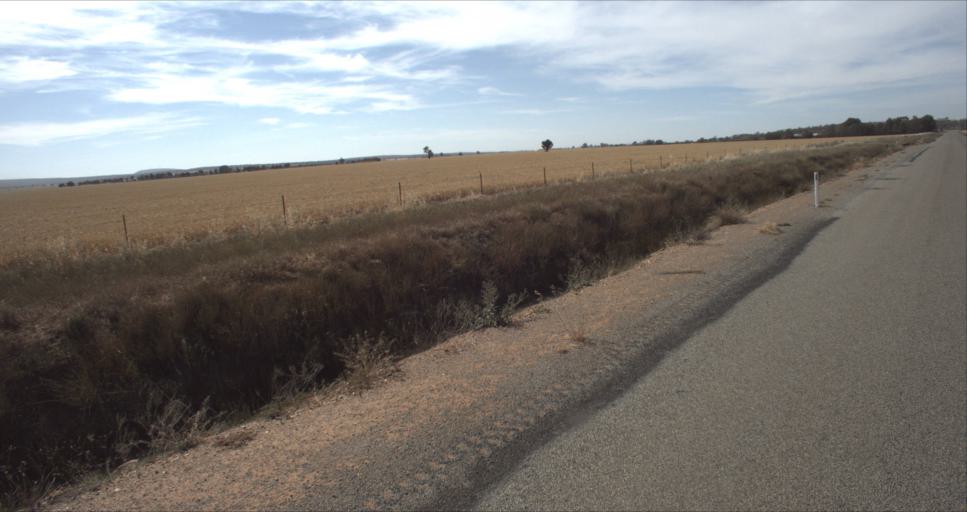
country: AU
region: New South Wales
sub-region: Leeton
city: Leeton
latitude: -34.5664
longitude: 146.4718
